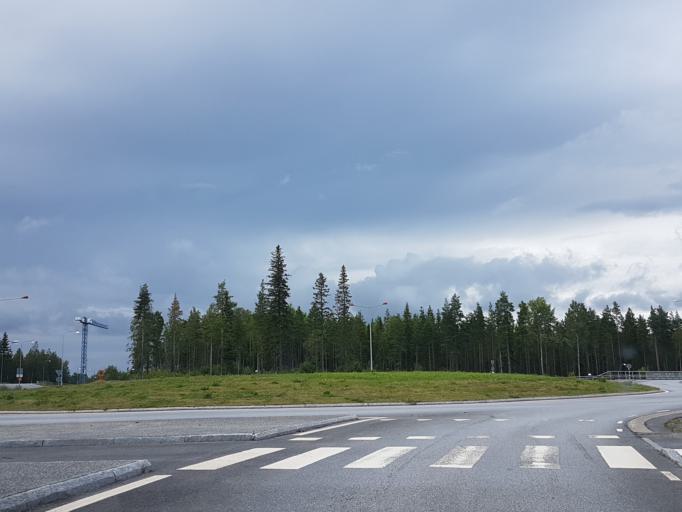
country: SE
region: Vaesterbotten
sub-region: Umea Kommun
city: Ersmark
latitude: 63.8024
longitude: 20.3627
